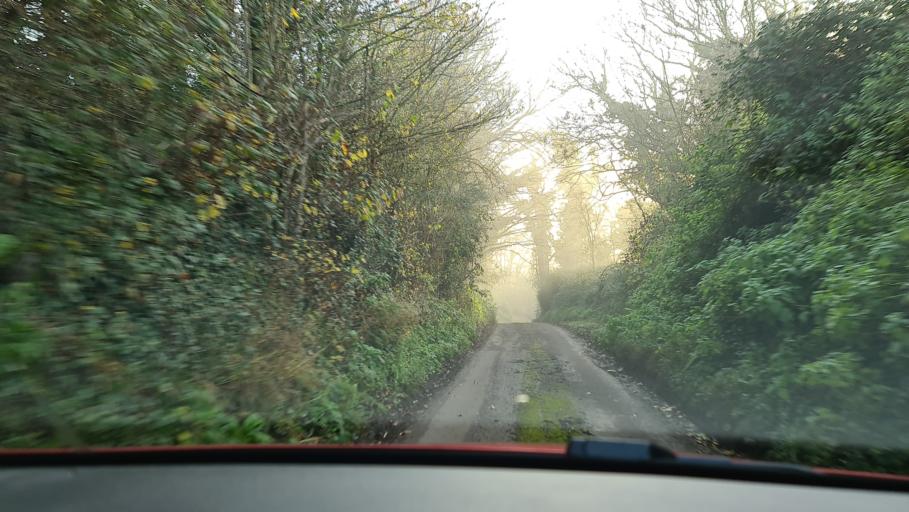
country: GB
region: England
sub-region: Buckinghamshire
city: Haddenham
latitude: 51.8062
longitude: -0.9416
